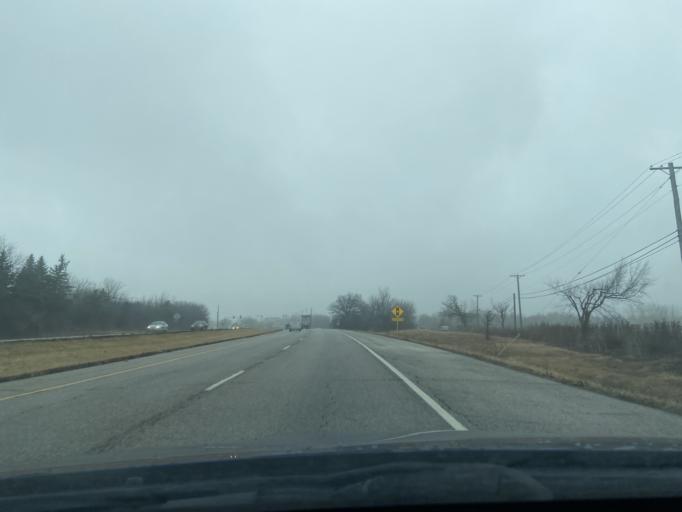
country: US
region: Illinois
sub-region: Lake County
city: Wauconda
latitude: 42.2349
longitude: -88.1115
